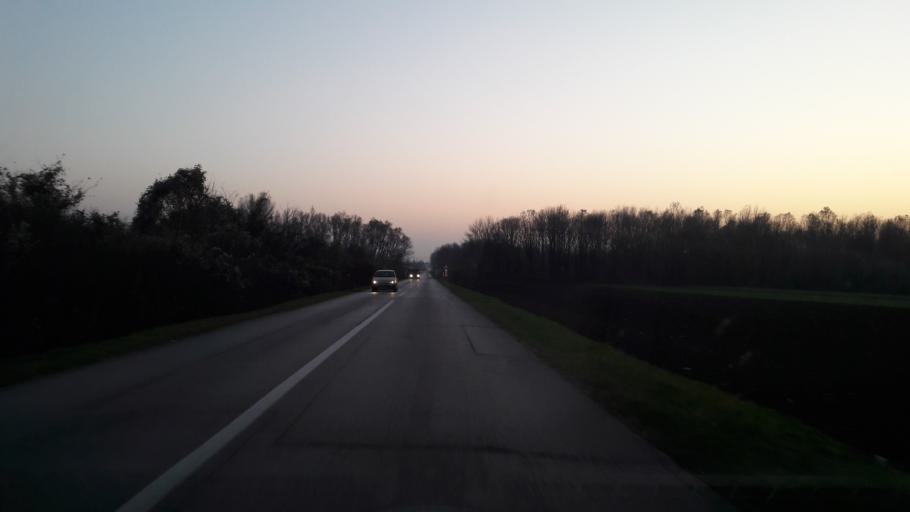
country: HR
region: Vukovarsko-Srijemska
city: Nijemci
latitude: 45.1966
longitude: 19.0217
